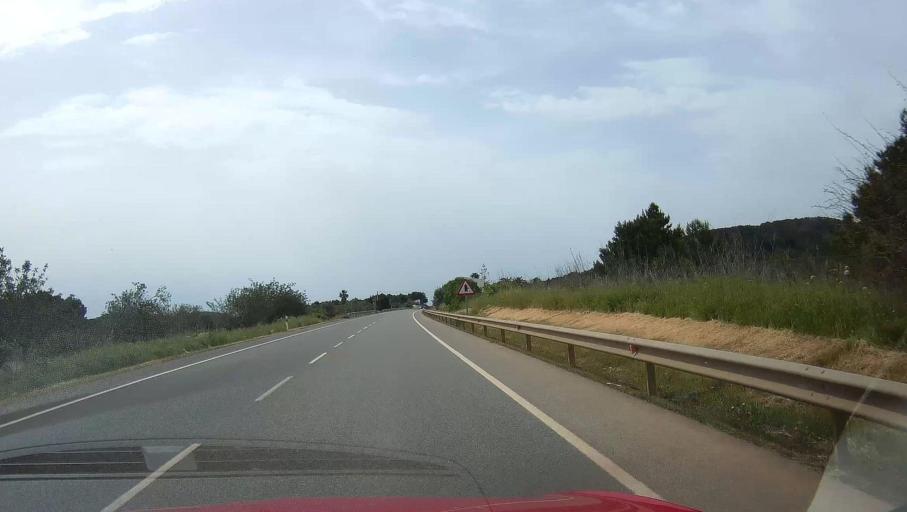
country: ES
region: Balearic Islands
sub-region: Illes Balears
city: Sant Joan de Labritja
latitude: 39.0486
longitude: 1.4910
